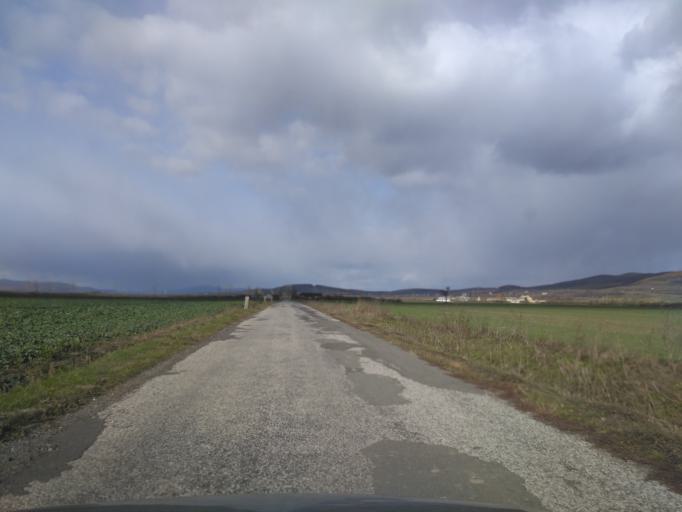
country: HU
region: Borsod-Abauj-Zemplen
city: Satoraljaujhely
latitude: 48.4161
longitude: 21.6788
